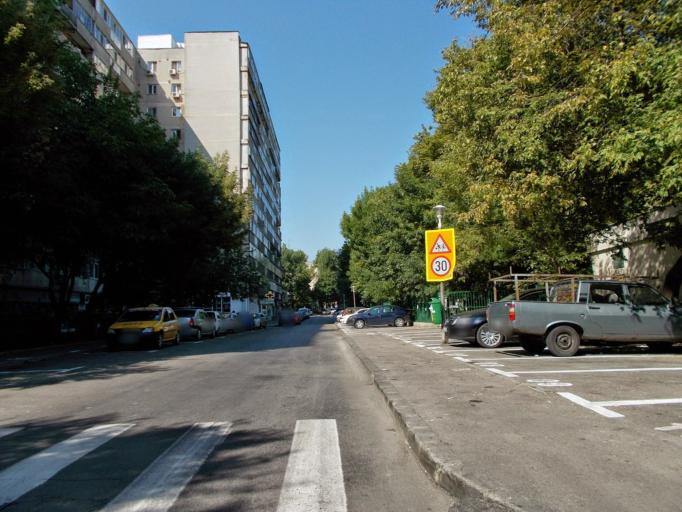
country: RO
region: Bucuresti
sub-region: Municipiul Bucuresti
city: Bucuresti
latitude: 44.3811
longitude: 26.1072
